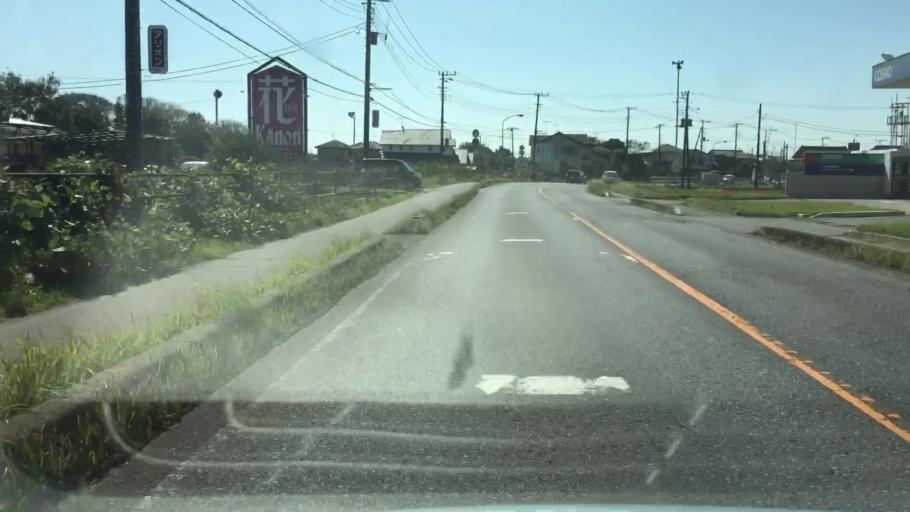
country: JP
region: Ibaraki
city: Ryugasaki
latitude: 35.8650
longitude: 140.1537
